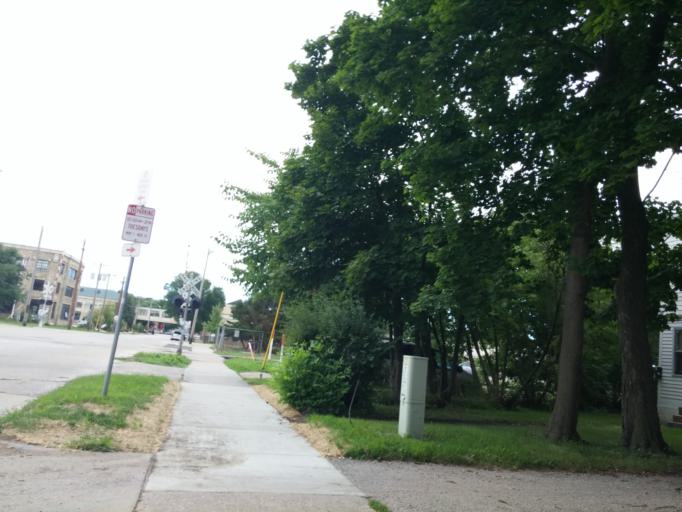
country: US
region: Wisconsin
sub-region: Dane County
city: Maple Bluff
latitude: 43.0856
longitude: -89.3639
